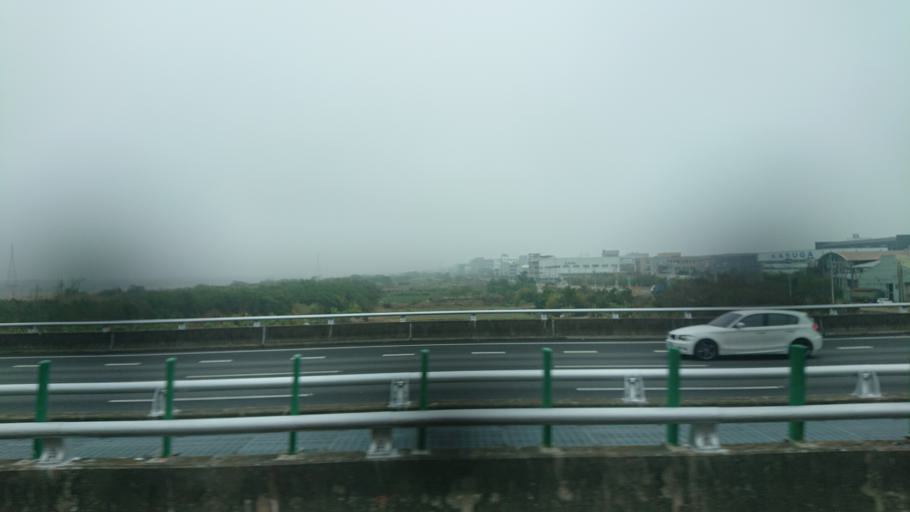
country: TW
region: Taiwan
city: Fengyuan
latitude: 24.2803
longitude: 120.6940
